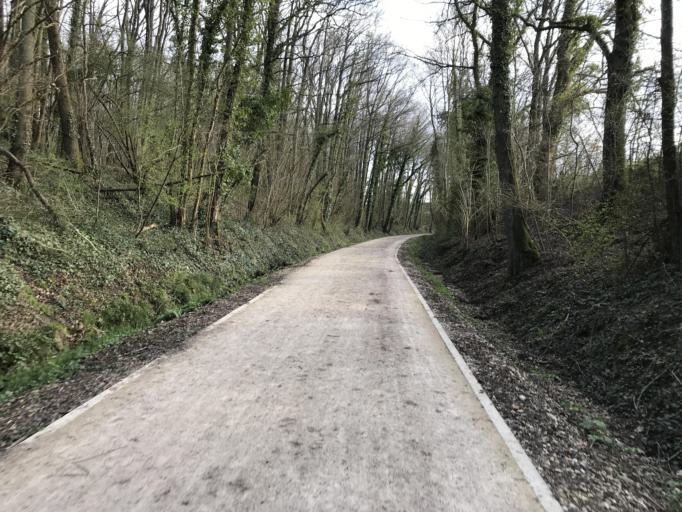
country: FR
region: Ile-de-France
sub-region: Departement de l'Essonne
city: Les Molieres
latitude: 48.6728
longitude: 2.0536
